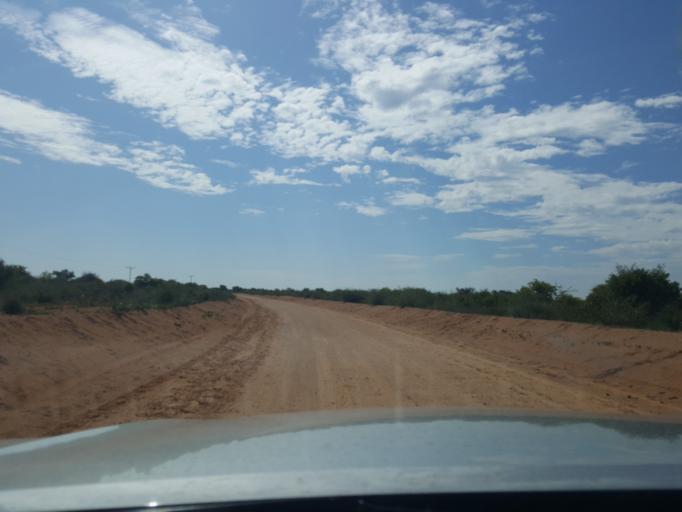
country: BW
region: Kweneng
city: Khudumelapye
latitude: -23.8522
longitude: 24.8738
